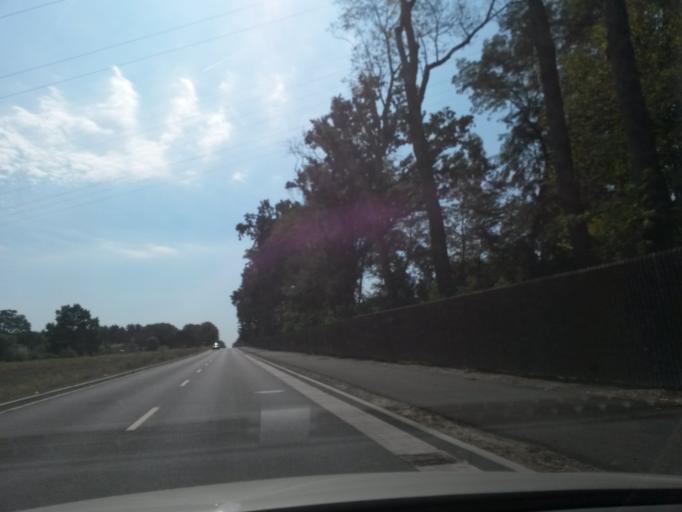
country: DE
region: Saxony-Anhalt
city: Jerichow
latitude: 52.4345
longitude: 11.9975
